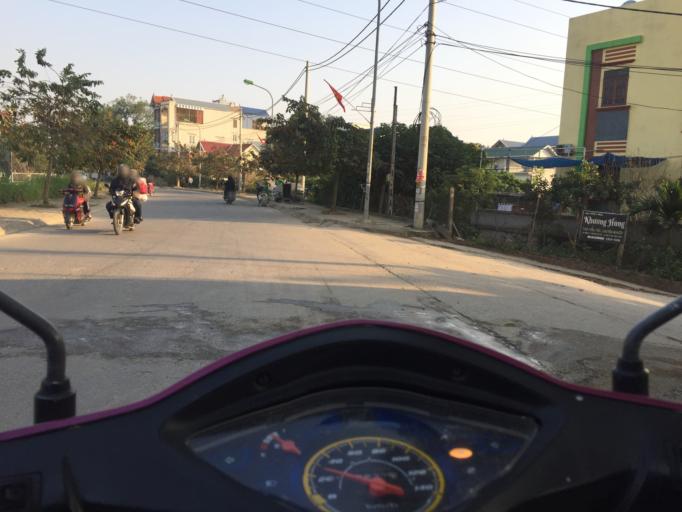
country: VN
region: Ha Noi
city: Chuc Son
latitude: 20.9214
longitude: 105.7104
